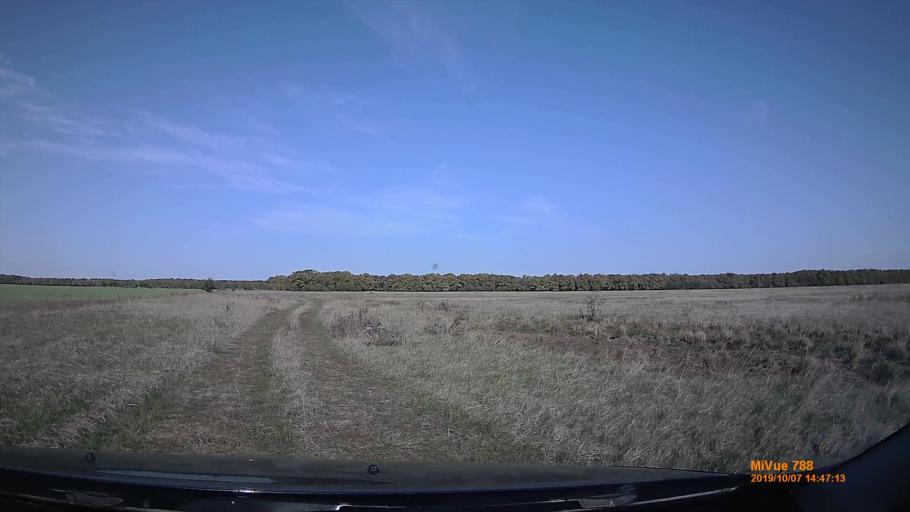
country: HU
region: Jasz-Nagykun-Szolnok
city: Kunszentmarton
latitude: 46.8551
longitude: 20.3200
